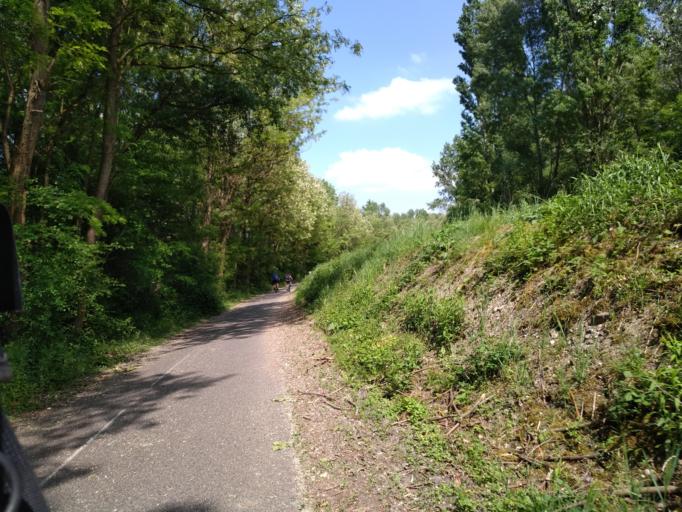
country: FR
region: Rhone-Alpes
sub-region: Departement du Rhone
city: Vaulx-en-Velin
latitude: 45.7910
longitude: 4.9030
